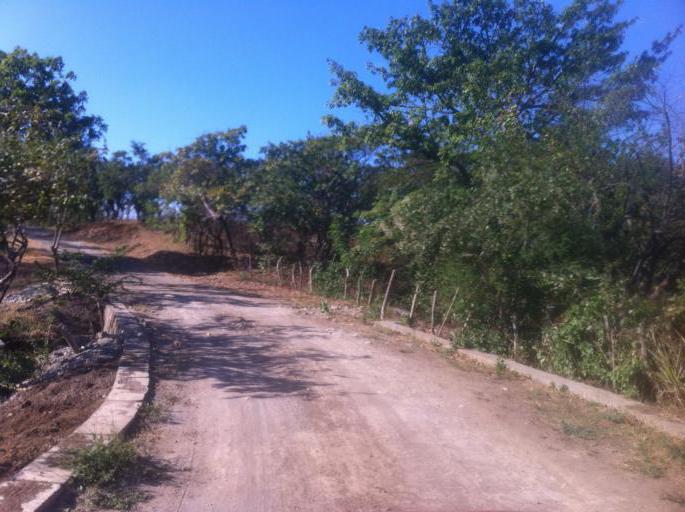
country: NI
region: Managua
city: Carlos Fonseca Amador
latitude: 11.9077
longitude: -86.6062
